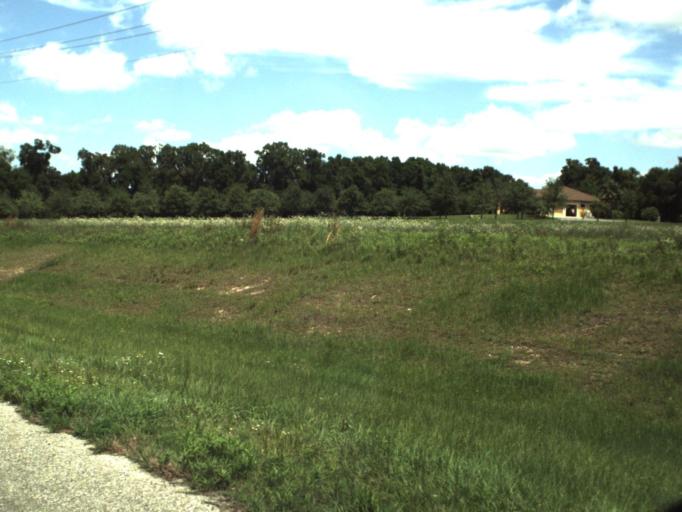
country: US
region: Florida
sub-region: Marion County
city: Citra
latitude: 29.3533
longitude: -82.1612
